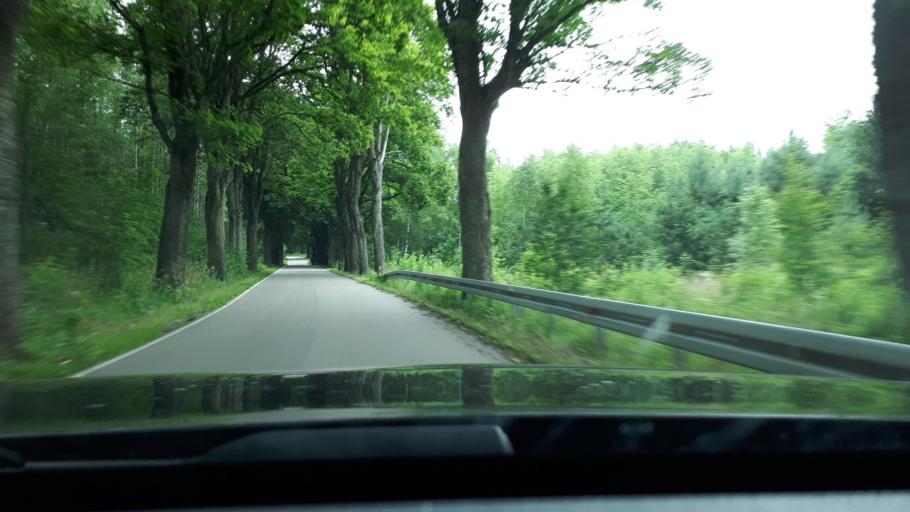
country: PL
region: Warmian-Masurian Voivodeship
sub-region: Powiat ostrodzki
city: Ostroda
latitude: 53.6843
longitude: 20.0678
